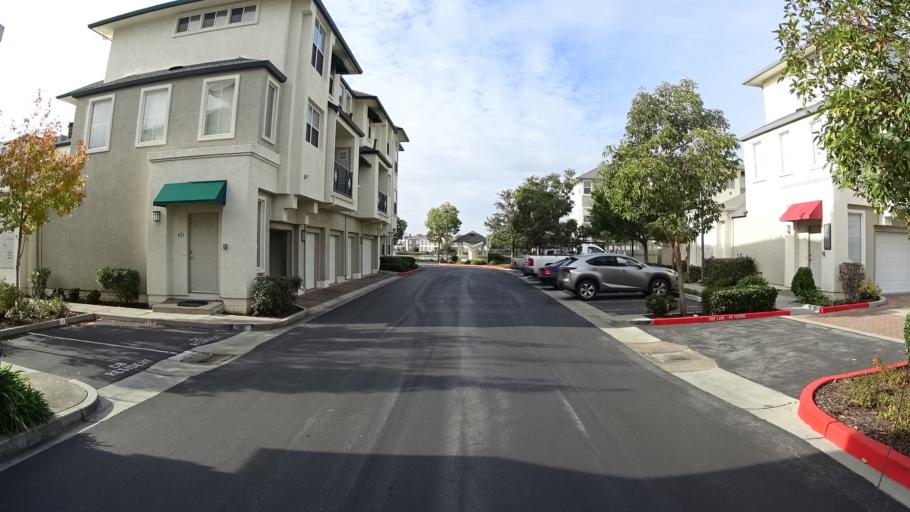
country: US
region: California
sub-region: San Mateo County
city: Redwood Shores
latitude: 37.5393
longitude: -122.2415
